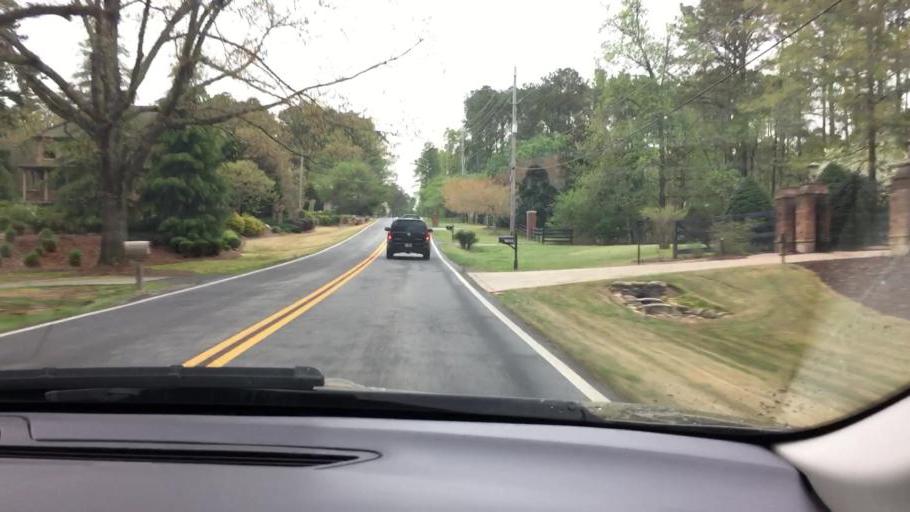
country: US
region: Georgia
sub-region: Fulton County
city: Milton
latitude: 34.1456
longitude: -84.2645
